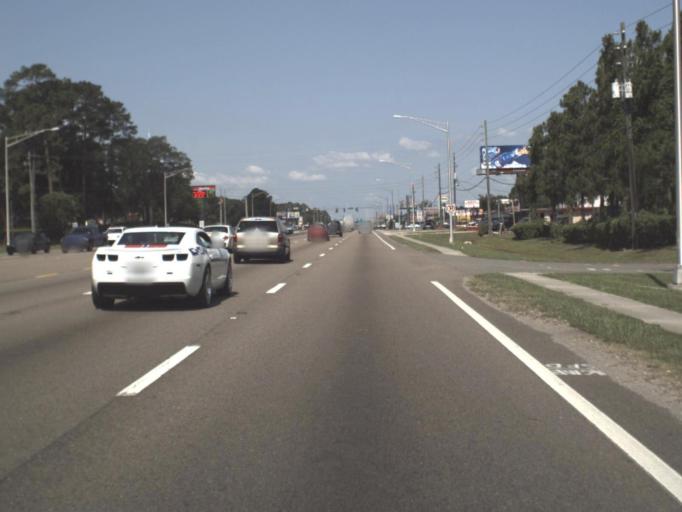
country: US
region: Florida
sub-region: Duval County
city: Jacksonville
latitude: 30.2869
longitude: -81.5412
